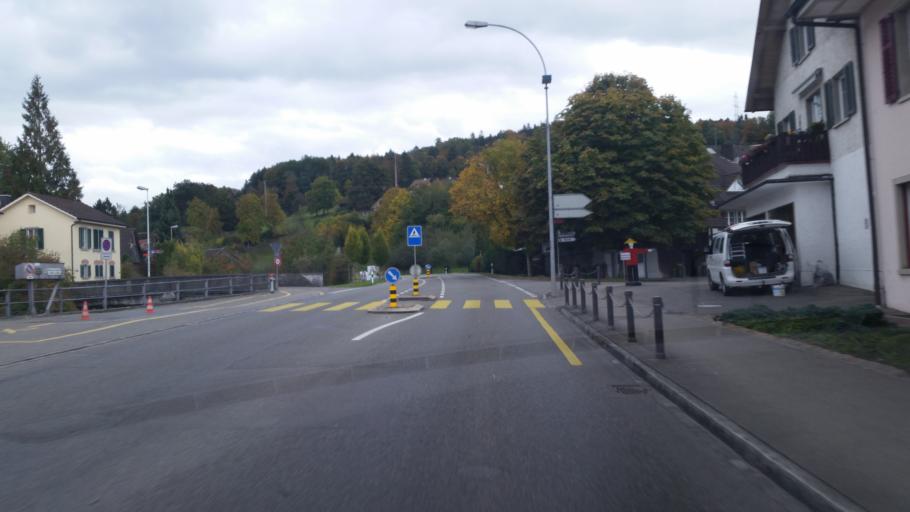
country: CH
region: Aargau
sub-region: Bezirk Zurzach
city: Oberendingen
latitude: 47.5369
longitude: 8.2907
